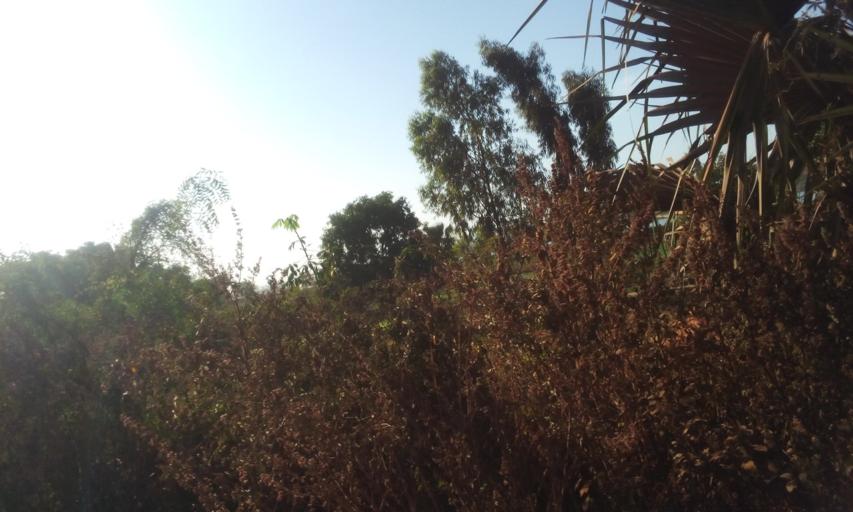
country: ML
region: Bamako
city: Bamako
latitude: 12.6462
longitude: -7.9035
